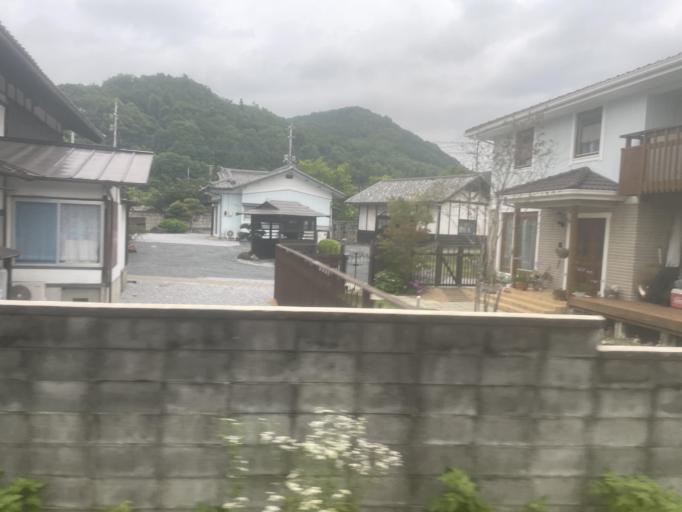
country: JP
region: Saitama
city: Yorii
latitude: 36.1004
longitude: 139.1101
